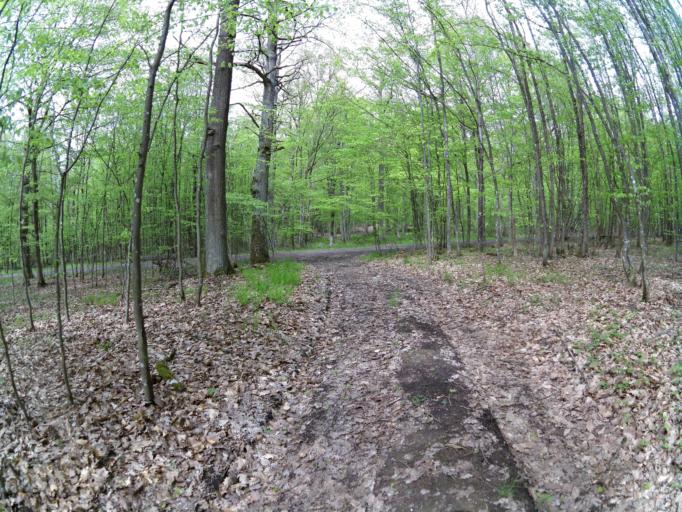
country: DE
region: Bavaria
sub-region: Regierungsbezirk Unterfranken
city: Prosselsheim
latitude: 49.8492
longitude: 10.1544
